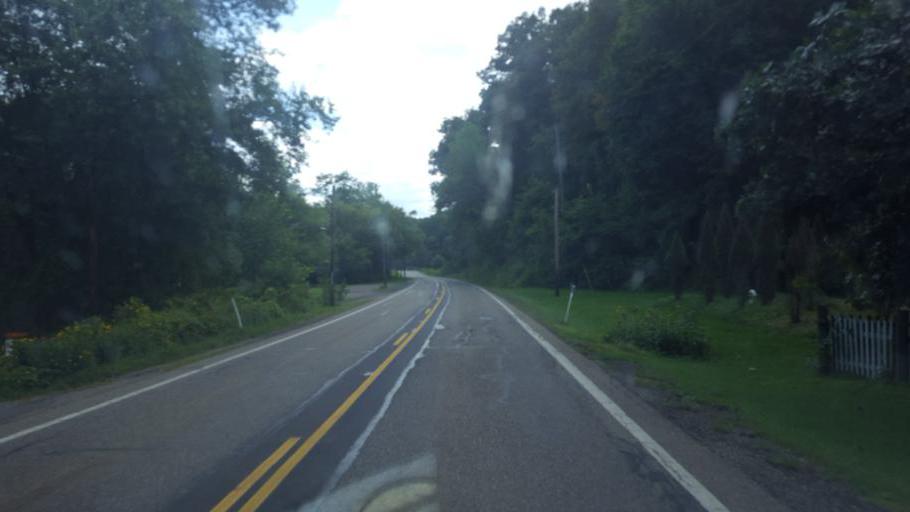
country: US
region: Ohio
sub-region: Tuscarawas County
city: Dover
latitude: 40.5486
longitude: -81.4252
